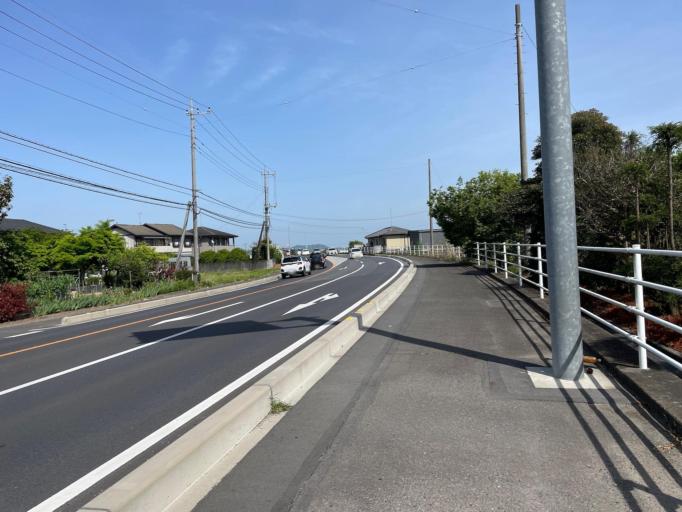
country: JP
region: Gunma
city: Tatebayashi
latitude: 36.3051
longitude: 139.5130
